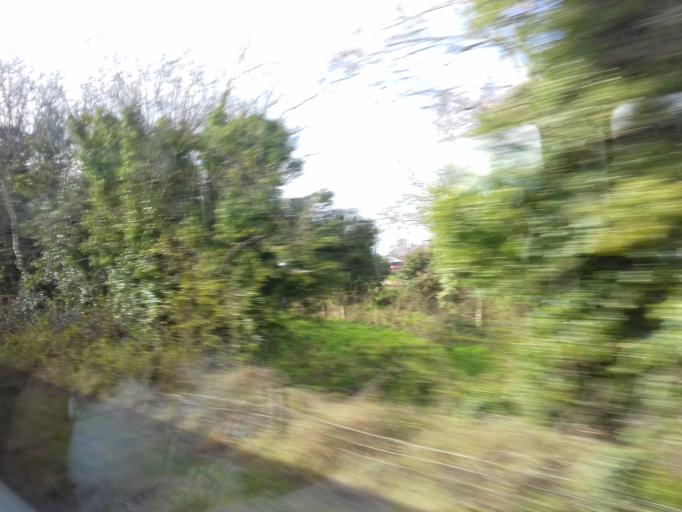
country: IE
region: Leinster
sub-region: An Iarmhi
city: Kinnegad
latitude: 53.4740
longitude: -7.0206
